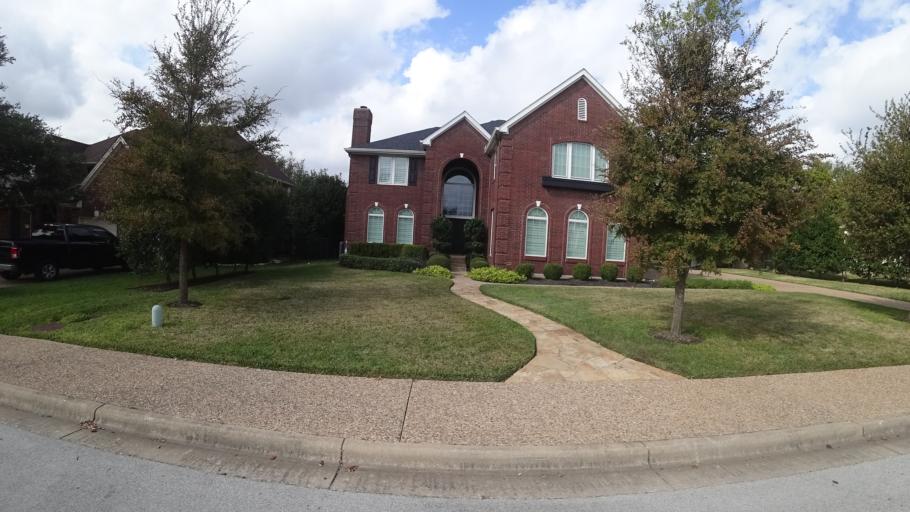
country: US
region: Texas
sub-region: Travis County
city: Barton Creek
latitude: 30.2943
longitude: -97.8974
